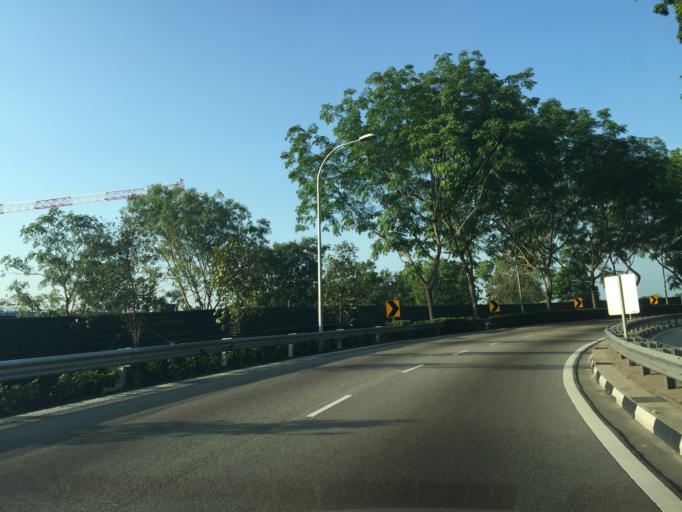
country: SG
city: Singapore
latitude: 1.3375
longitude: 103.9815
